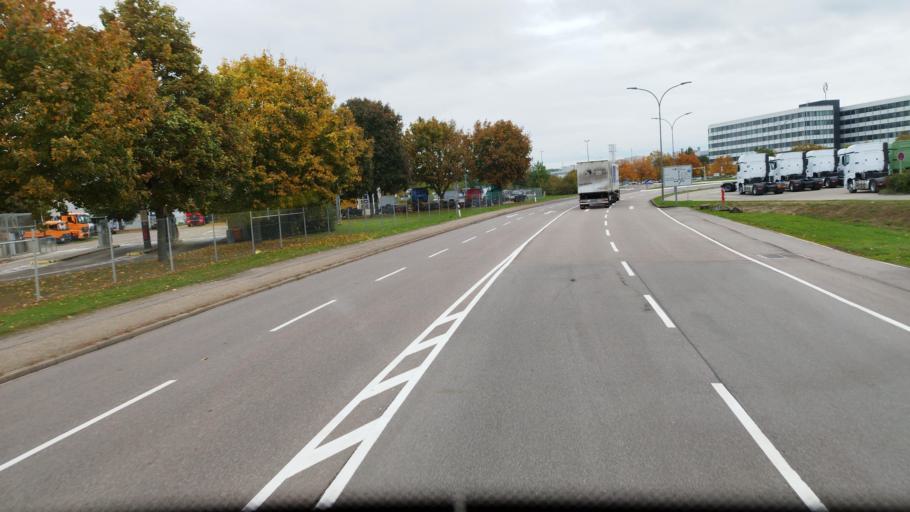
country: DE
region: Rheinland-Pfalz
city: Worth am Rhein
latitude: 49.0518
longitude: 8.2794
